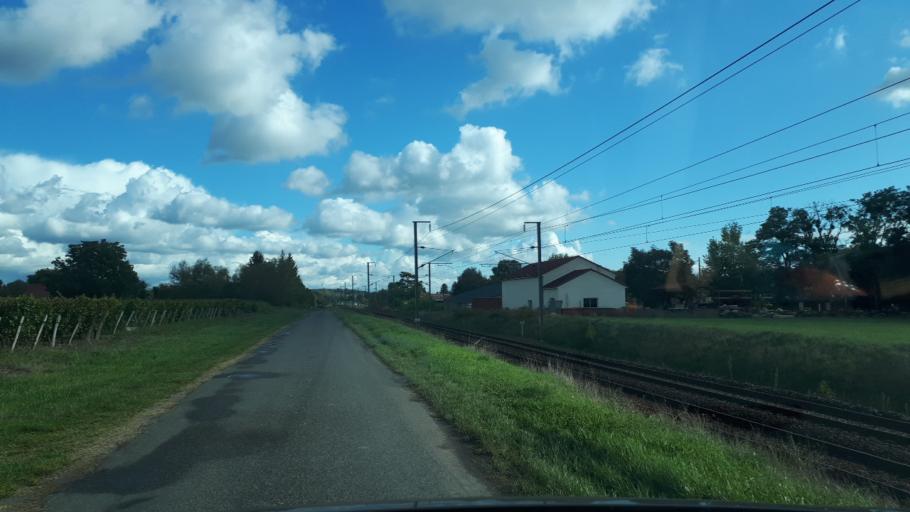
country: FR
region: Centre
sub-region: Departement du Loir-et-Cher
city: Thesee
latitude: 47.3174
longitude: 1.3257
